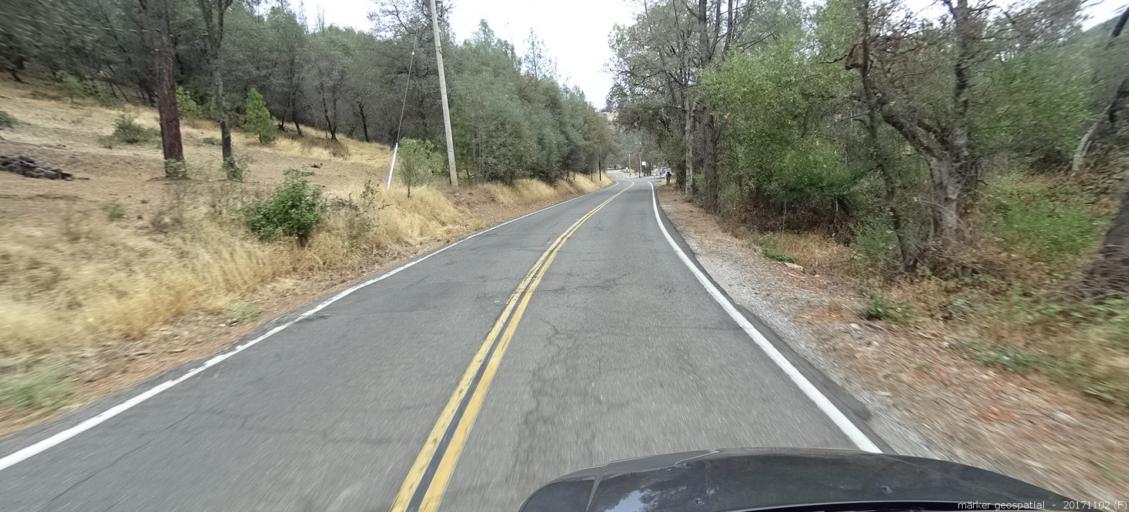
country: US
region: California
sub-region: Shasta County
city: Bella Vista
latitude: 40.7214
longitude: -122.2386
